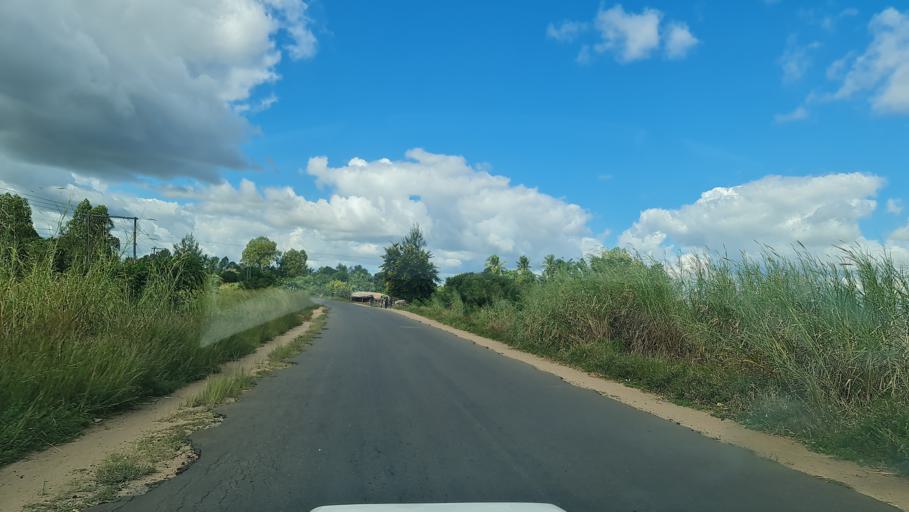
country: MZ
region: Zambezia
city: Quelimane
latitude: -17.6008
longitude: 36.8014
